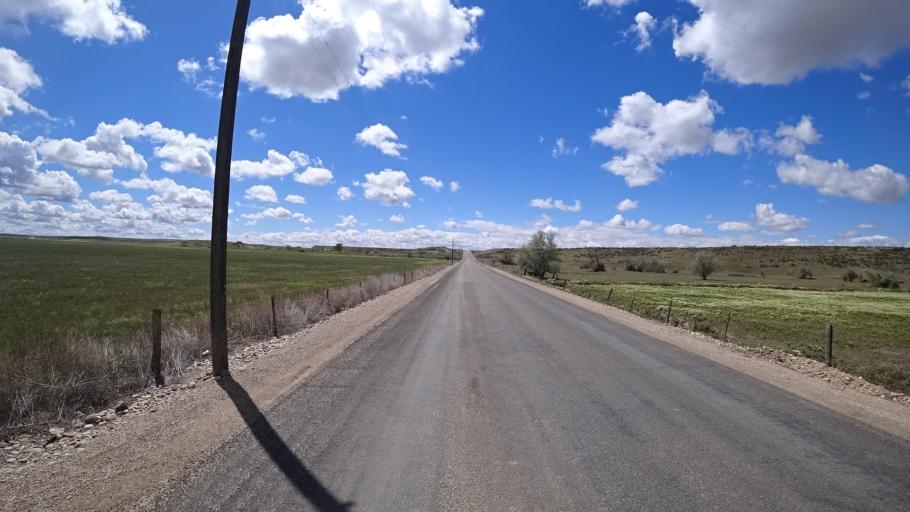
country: US
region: Idaho
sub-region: Ada County
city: Garden City
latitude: 43.4924
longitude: -116.2743
